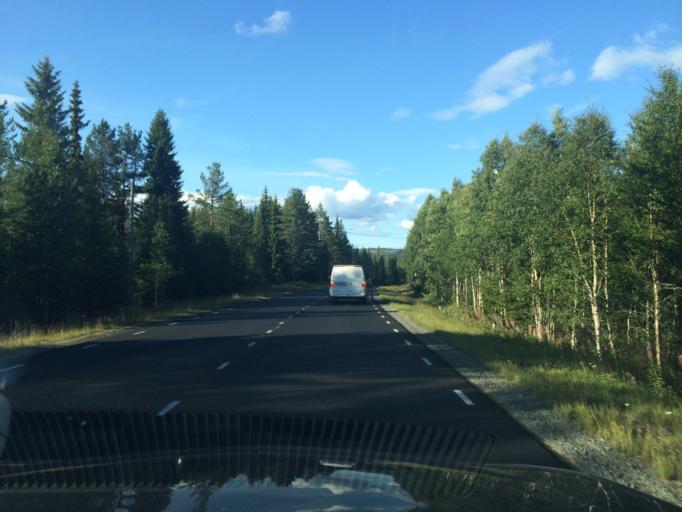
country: NO
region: Hedmark
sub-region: Trysil
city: Innbygda
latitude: 61.0825
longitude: 11.9808
